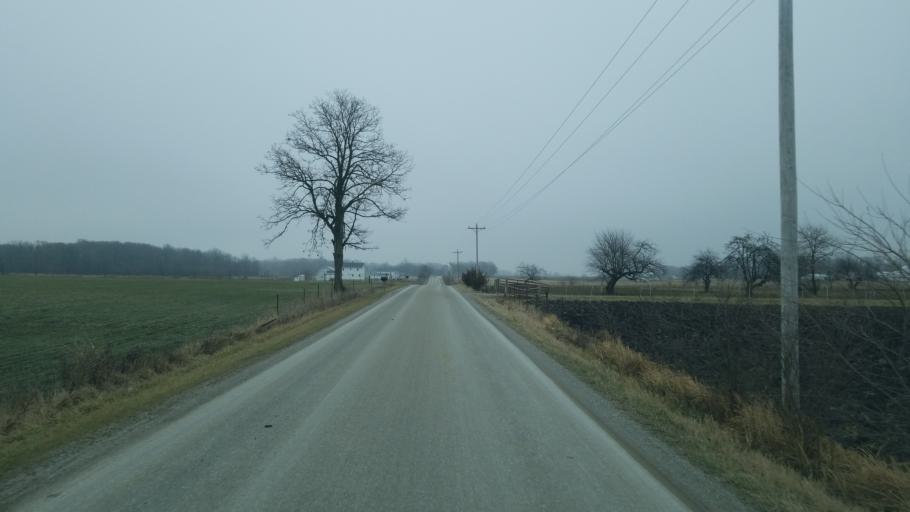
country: US
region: Indiana
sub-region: Adams County
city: Berne
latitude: 40.6438
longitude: -84.9253
